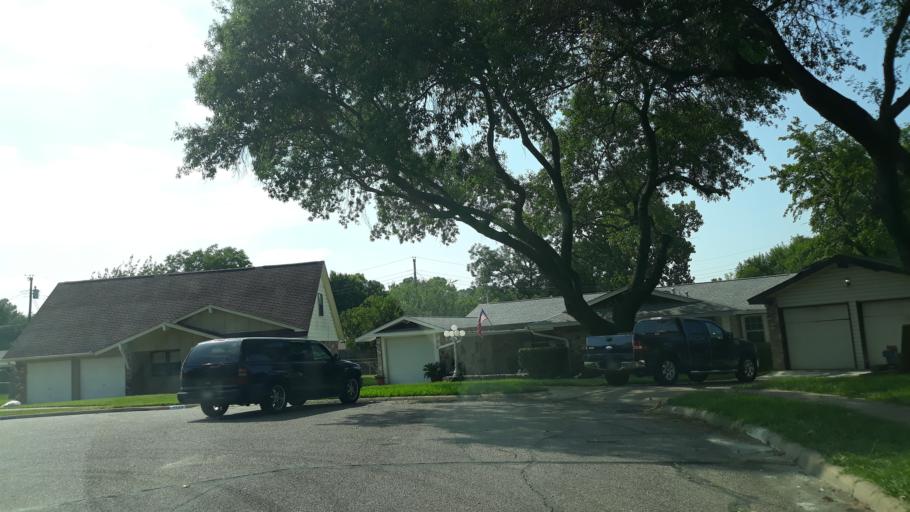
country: US
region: Texas
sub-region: Dallas County
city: Irving
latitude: 32.8419
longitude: -97.0044
